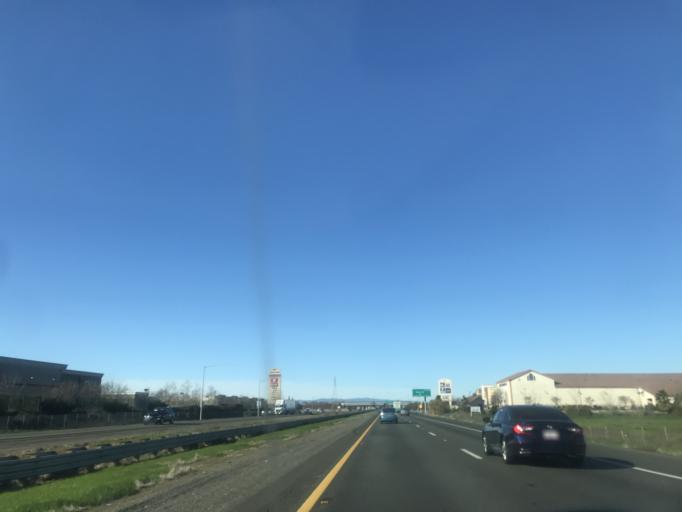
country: US
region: California
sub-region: Yolo County
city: Woodland
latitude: 38.6739
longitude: -121.7208
